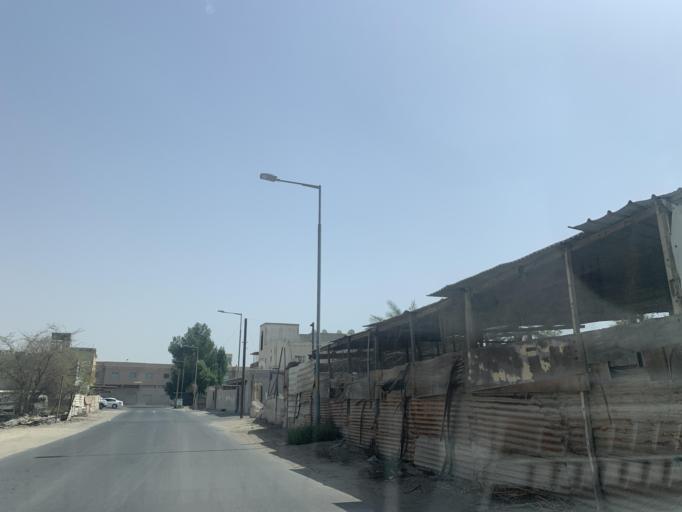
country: BH
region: Central Governorate
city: Madinat Hamad
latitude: 26.1467
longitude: 50.4951
